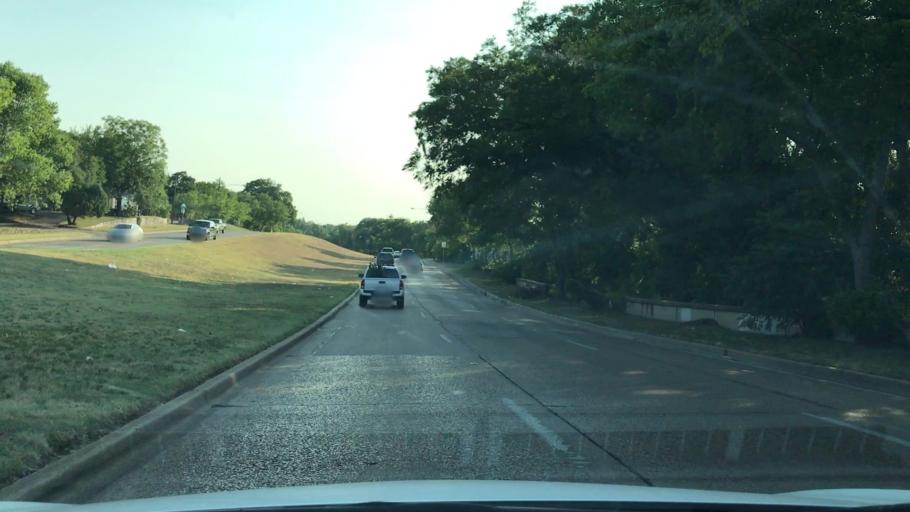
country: US
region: Texas
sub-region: Dallas County
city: Cockrell Hill
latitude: 32.7470
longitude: -96.8644
